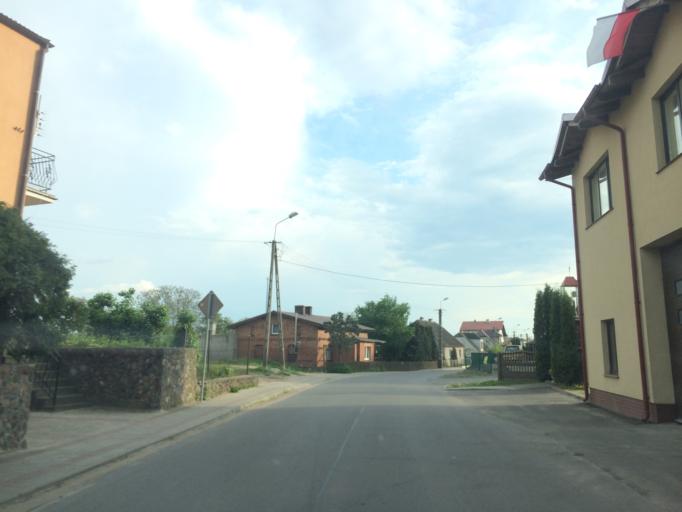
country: PL
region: Kujawsko-Pomorskie
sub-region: Powiat brodnicki
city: Brzozie
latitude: 53.3559
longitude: 19.7067
